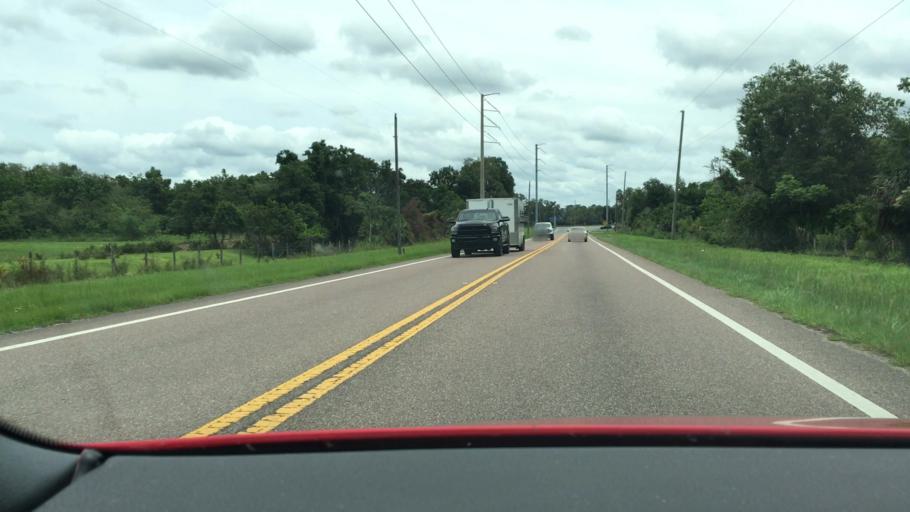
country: US
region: Florida
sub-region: Lake County
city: Eustis
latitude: 28.8753
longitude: -81.6747
